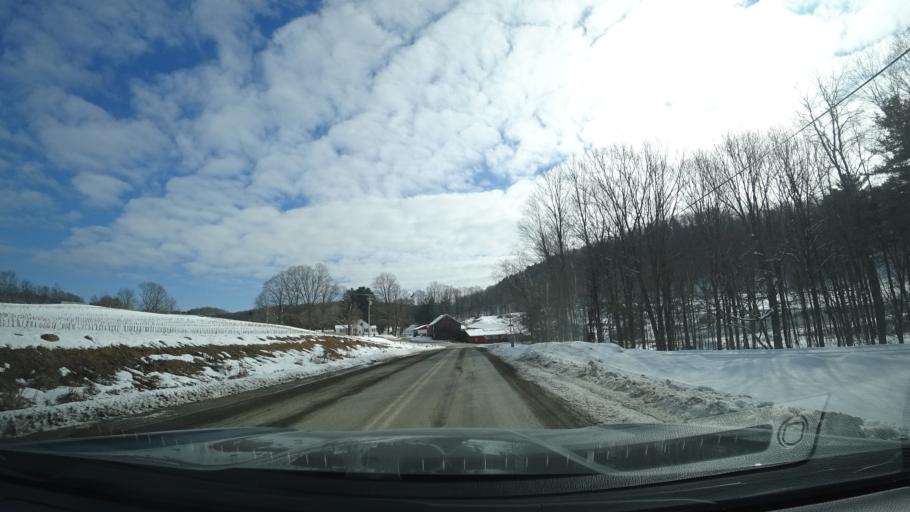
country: US
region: New York
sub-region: Washington County
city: Fort Edward
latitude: 43.2429
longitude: -73.4359
